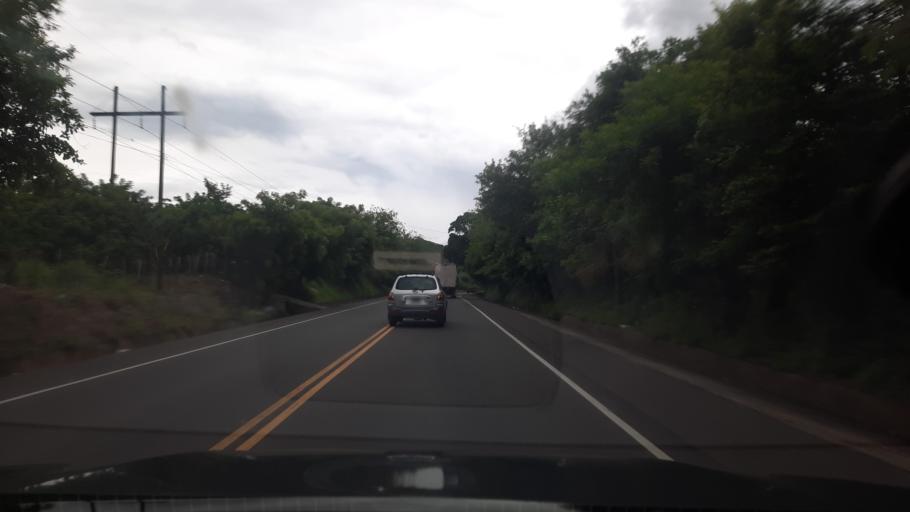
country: HN
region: Choluteca
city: Marcovia
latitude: 13.3686
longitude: -87.2899
